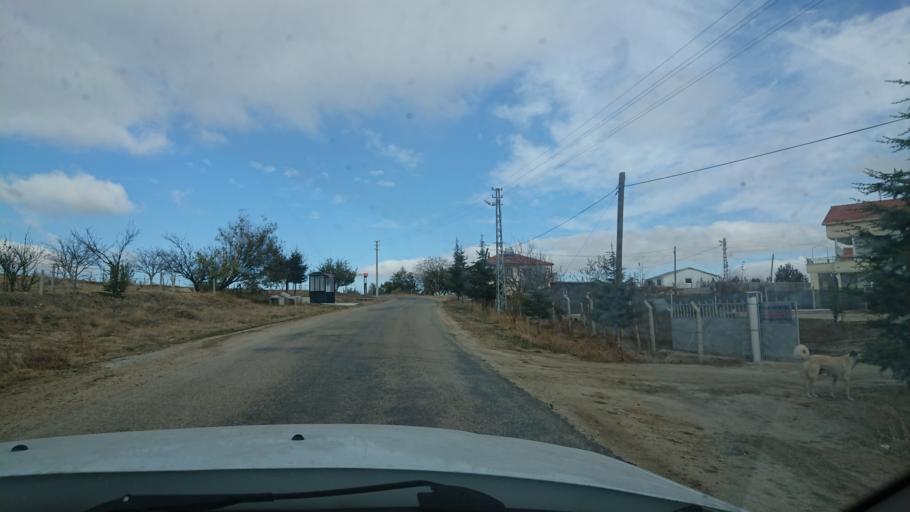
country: TR
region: Aksaray
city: Agacoren
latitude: 38.8261
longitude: 33.9578
